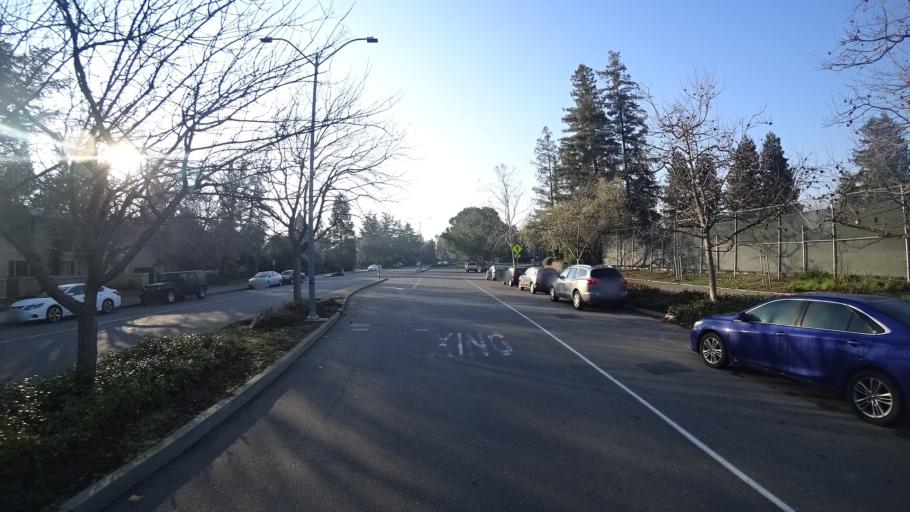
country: US
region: California
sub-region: Yolo County
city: Davis
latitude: 38.5523
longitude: -121.7875
